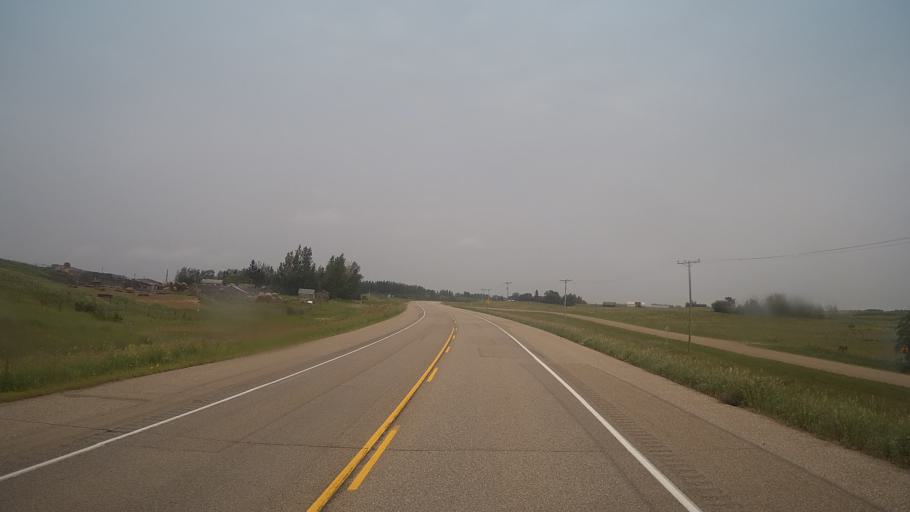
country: CA
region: Saskatchewan
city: Biggar
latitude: 52.0581
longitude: -107.8944
